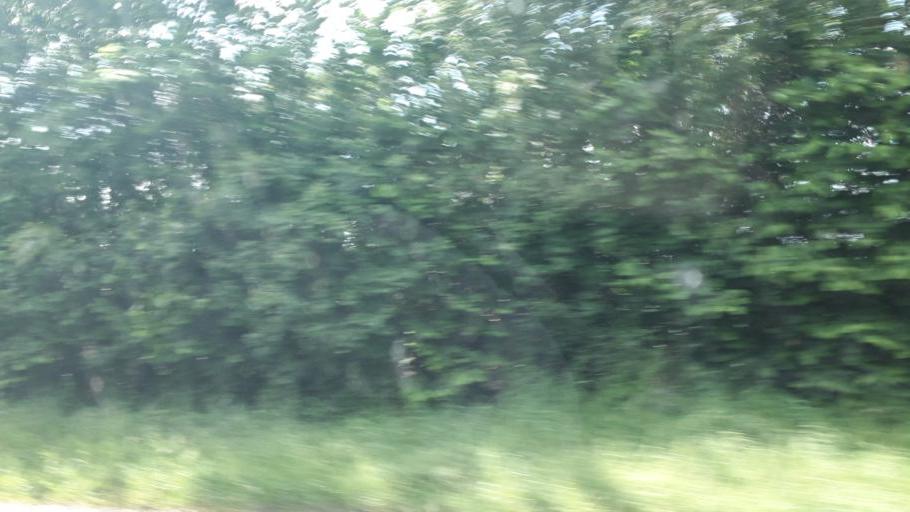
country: IE
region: Leinster
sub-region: Kildare
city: Moone
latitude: 53.0054
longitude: -6.8045
